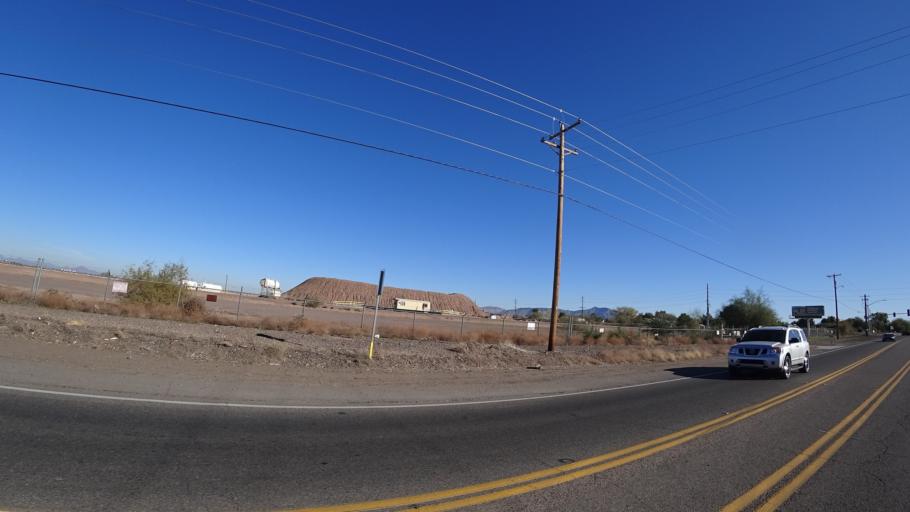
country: US
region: Arizona
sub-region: Maricopa County
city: Laveen
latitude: 33.3935
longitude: -112.2031
